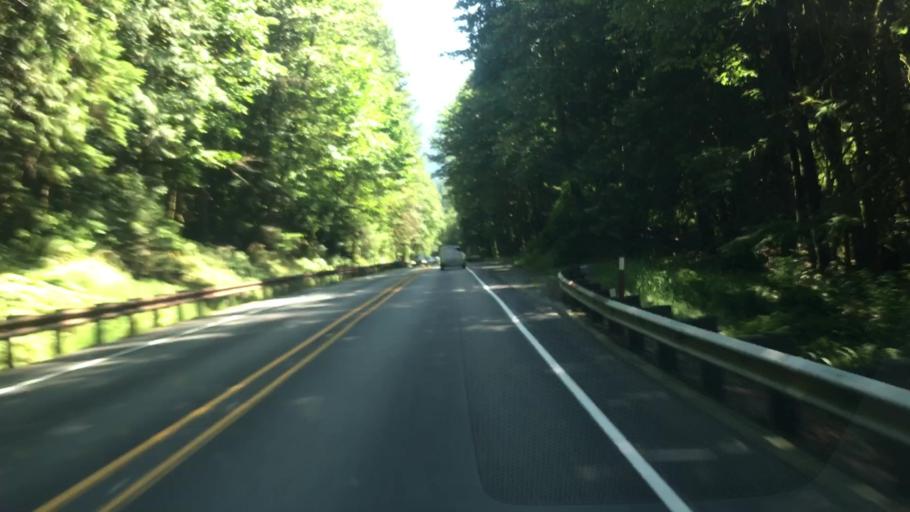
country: US
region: Washington
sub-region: Snohomish County
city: Gold Bar
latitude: 47.7252
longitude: -121.3951
